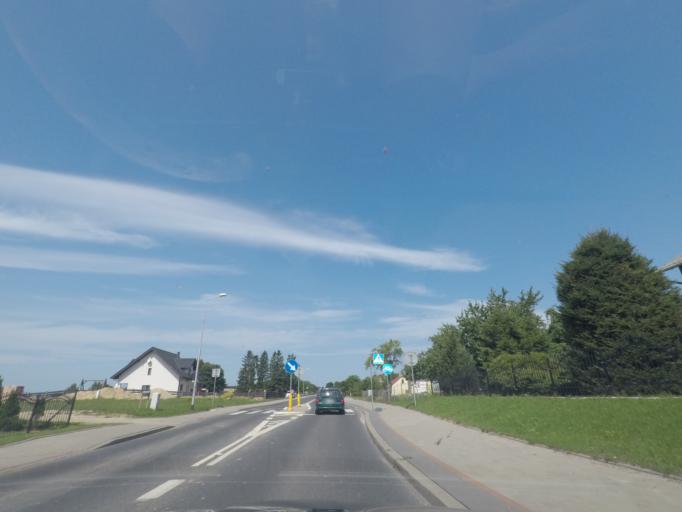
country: PL
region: West Pomeranian Voivodeship
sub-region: Powiat koszalinski
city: Sianow
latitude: 54.2537
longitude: 16.2764
